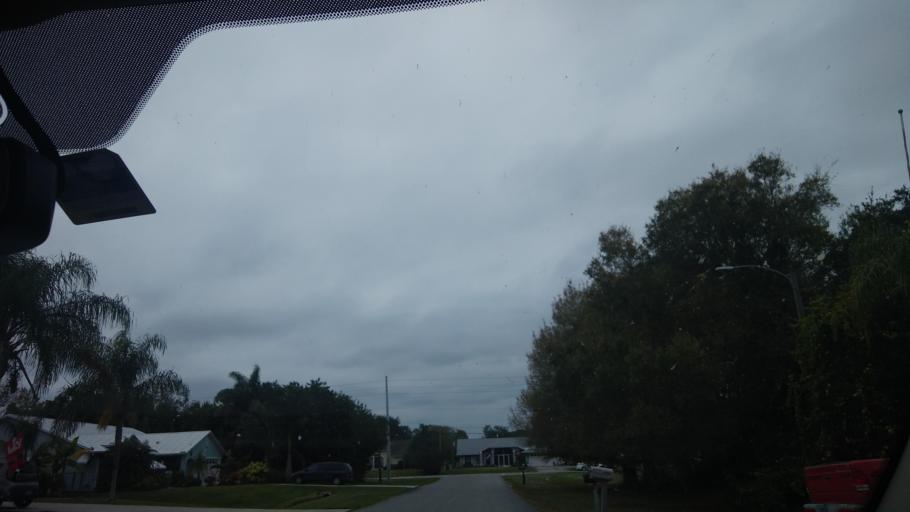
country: US
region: Florida
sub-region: Indian River County
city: Sebastian
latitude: 27.7732
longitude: -80.4972
